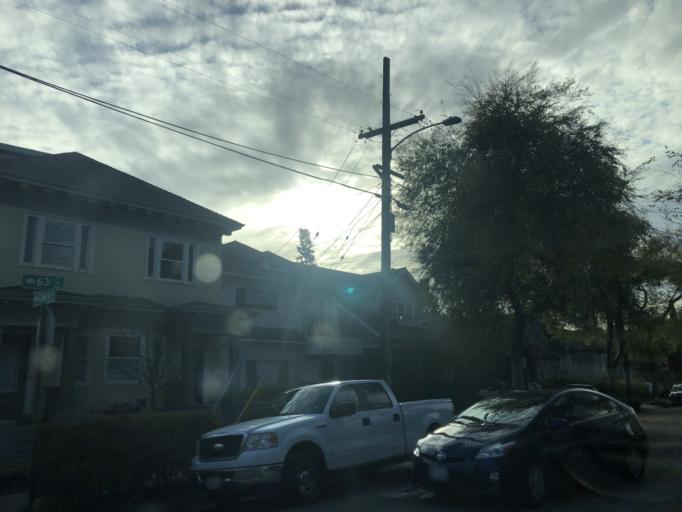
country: US
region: California
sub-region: Alameda County
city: Berkeley
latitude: 37.8493
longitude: -122.2569
